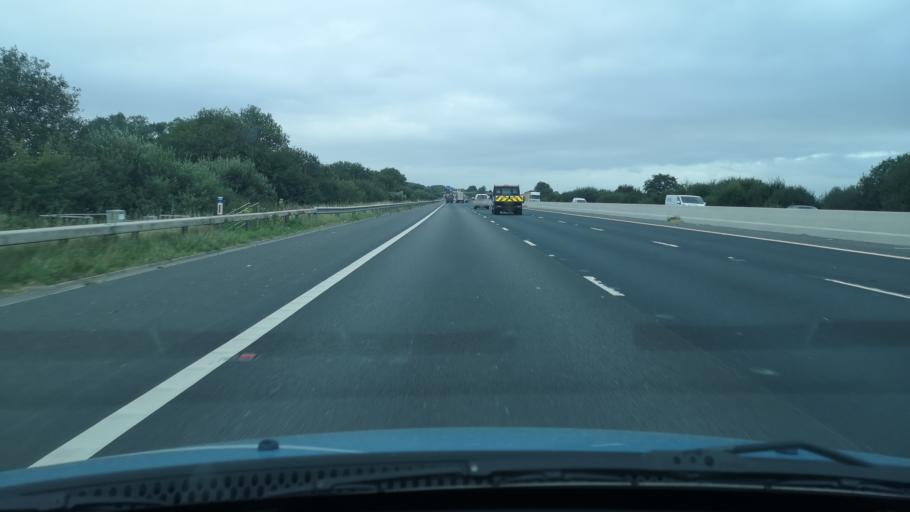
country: GB
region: England
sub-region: City and Borough of Wakefield
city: Knottingley
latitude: 53.6942
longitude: -1.2110
